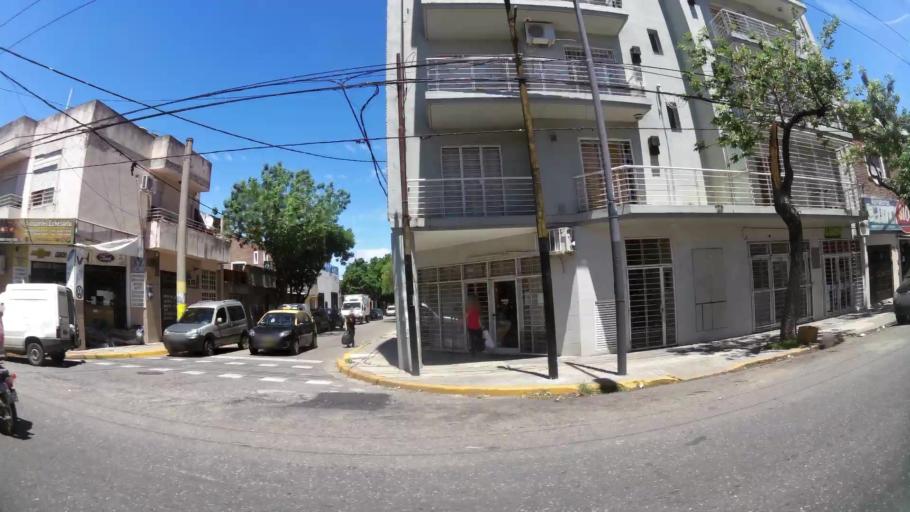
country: AR
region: Santa Fe
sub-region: Departamento de Rosario
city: Rosario
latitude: -32.9426
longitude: -60.6894
